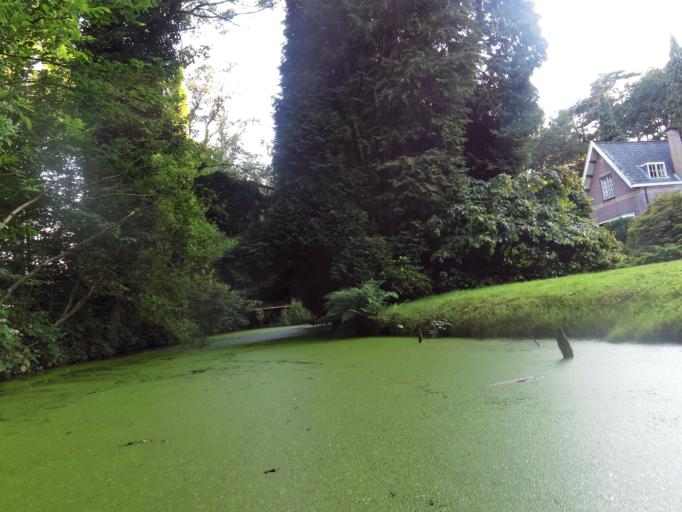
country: NL
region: South Holland
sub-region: Gemeente Wassenaar
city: Wassenaar
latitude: 52.1339
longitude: 4.3845
